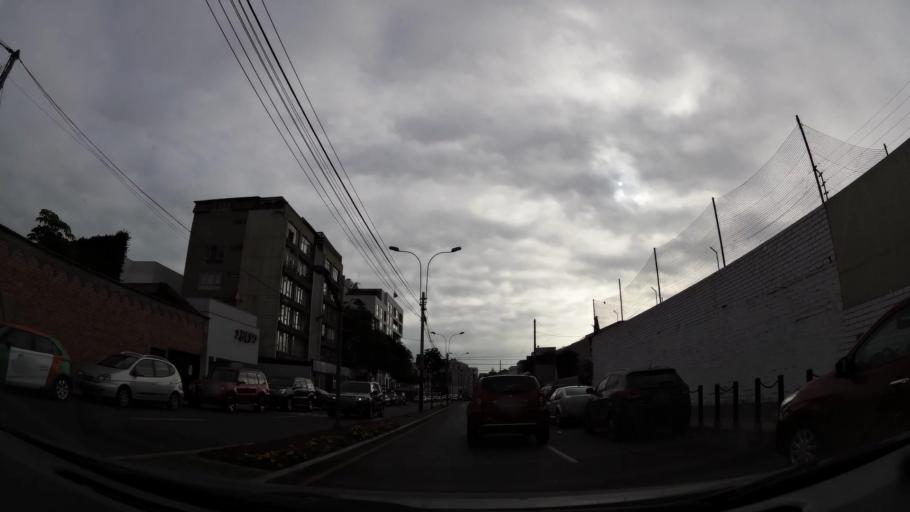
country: PE
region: Lima
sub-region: Lima
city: San Isidro
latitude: -12.1026
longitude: -77.0534
